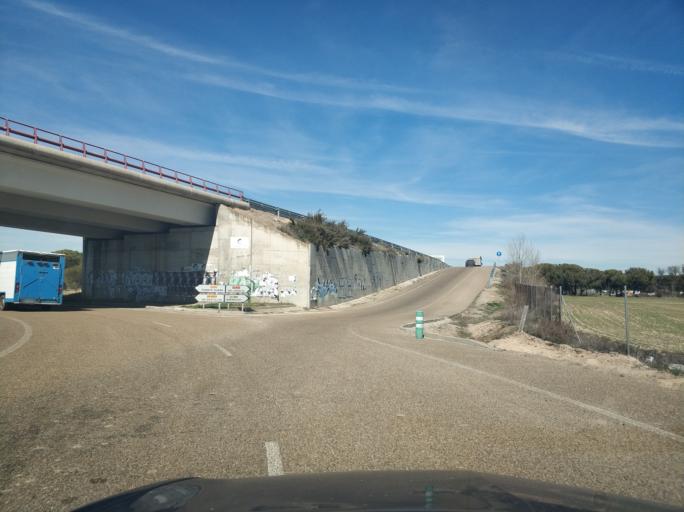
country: ES
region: Castille and Leon
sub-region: Provincia de Valladolid
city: Viana de Cega
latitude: 41.5489
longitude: -4.7872
